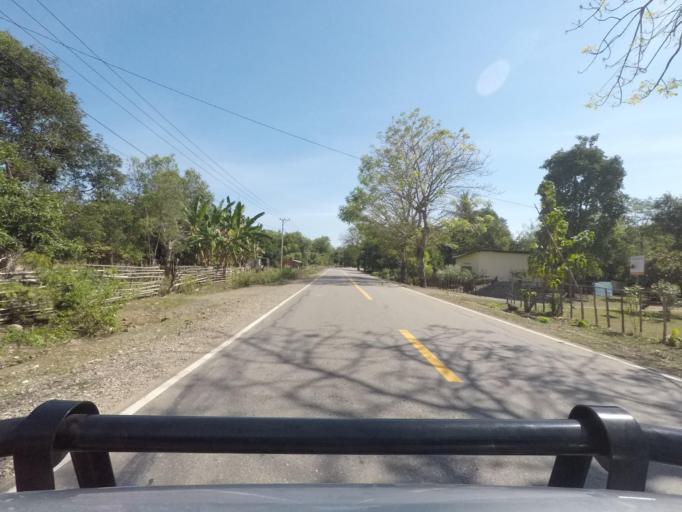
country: TL
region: Bobonaro
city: Maliana
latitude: -8.8943
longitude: 125.0084
